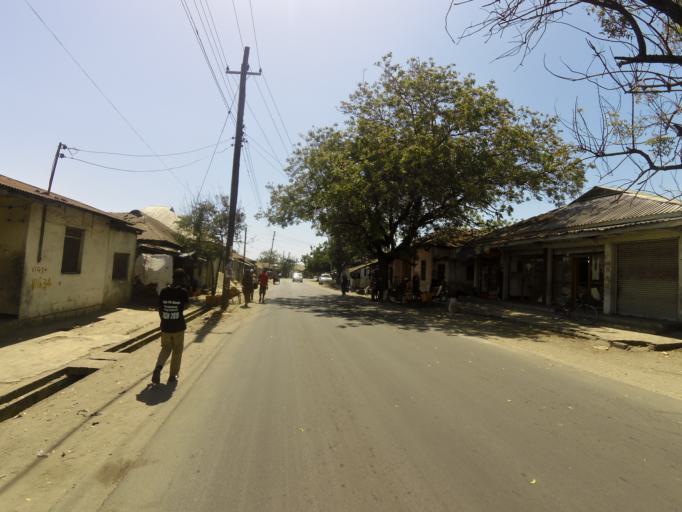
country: TZ
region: Dar es Salaam
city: Magomeni
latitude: -6.8005
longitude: 39.2526
